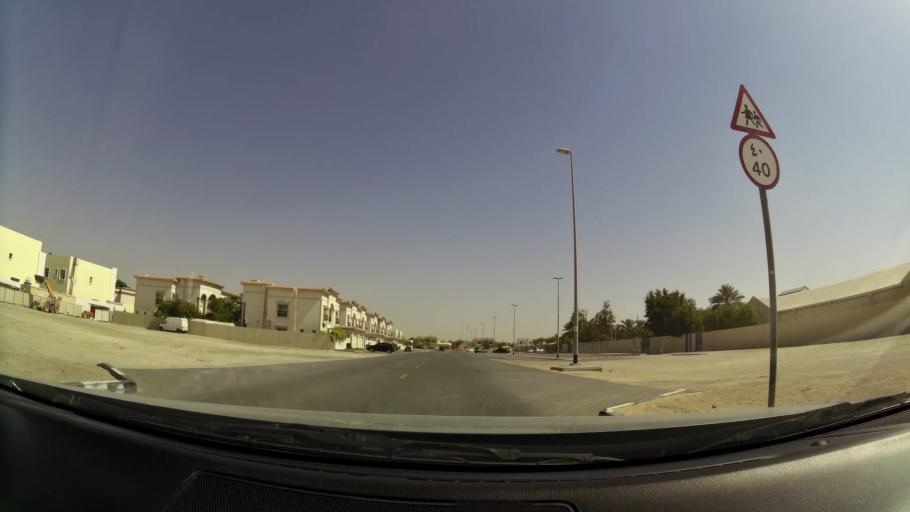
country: AE
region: Dubai
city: Dubai
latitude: 25.1080
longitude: 55.1938
